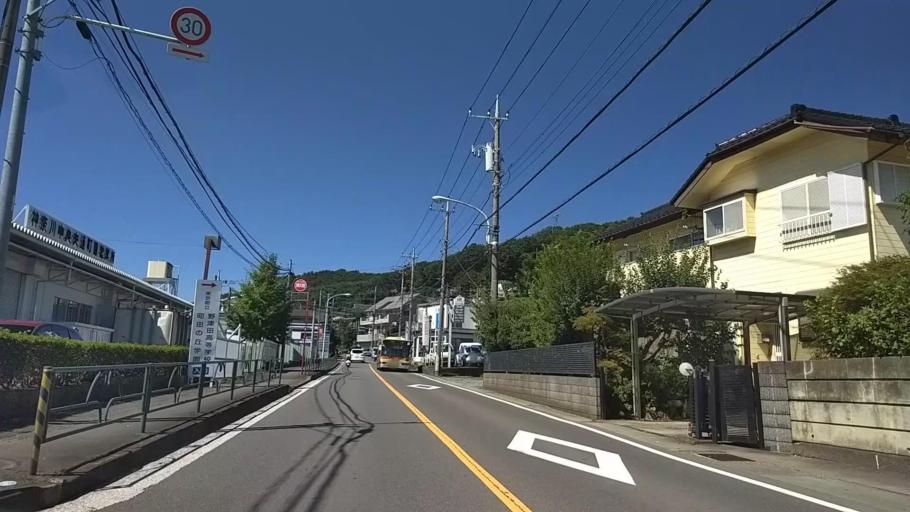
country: JP
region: Tokyo
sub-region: Machida-shi
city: Machida
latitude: 35.5872
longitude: 139.4414
